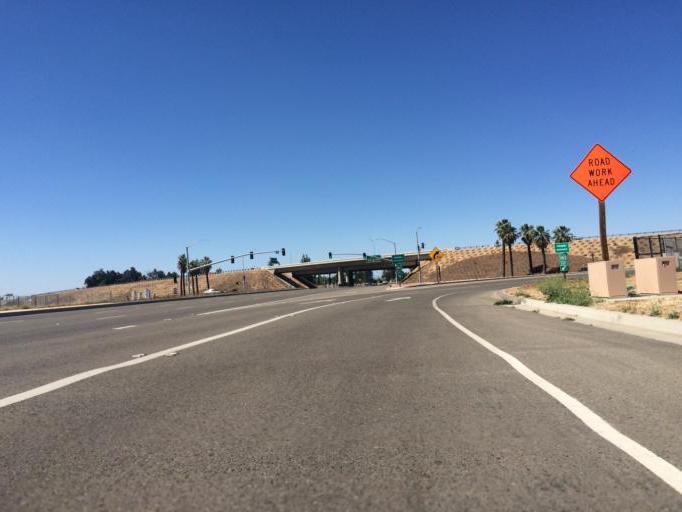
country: US
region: California
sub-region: Fresno County
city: Sunnyside
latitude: 36.7374
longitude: -119.6638
